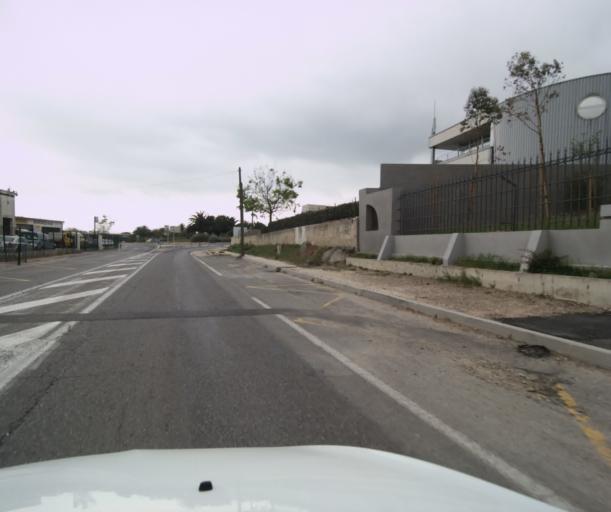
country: FR
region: Provence-Alpes-Cote d'Azur
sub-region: Departement du Var
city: La Crau
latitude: 43.1260
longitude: 6.0931
